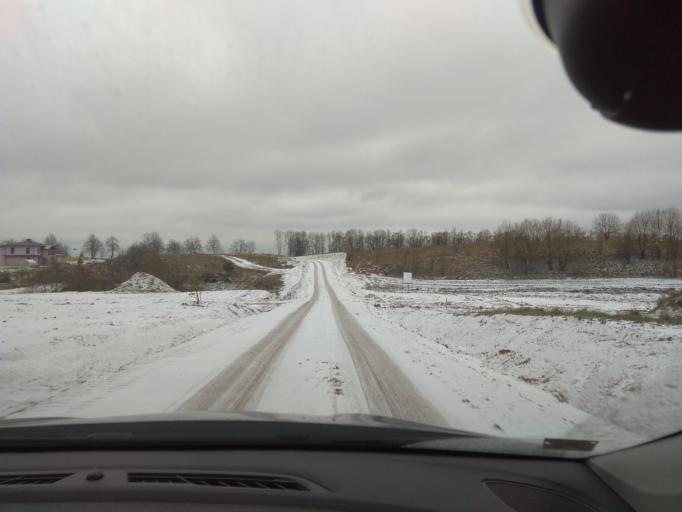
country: LT
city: Lentvaris
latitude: 54.6461
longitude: 25.0829
